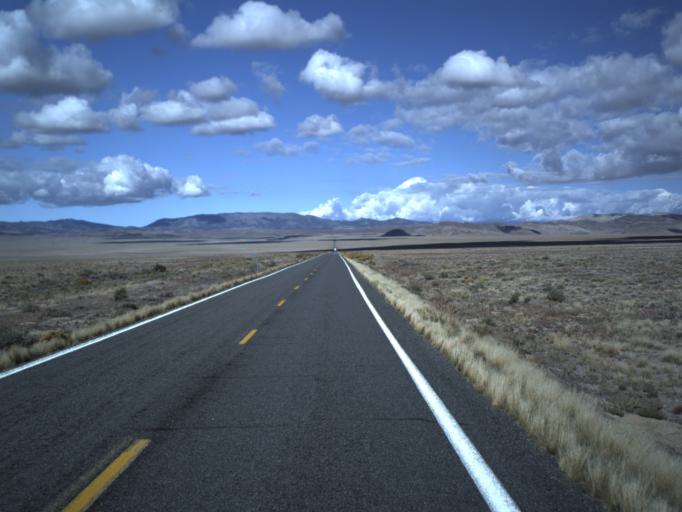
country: US
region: Utah
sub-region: Beaver County
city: Milford
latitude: 38.5371
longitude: -113.6948
